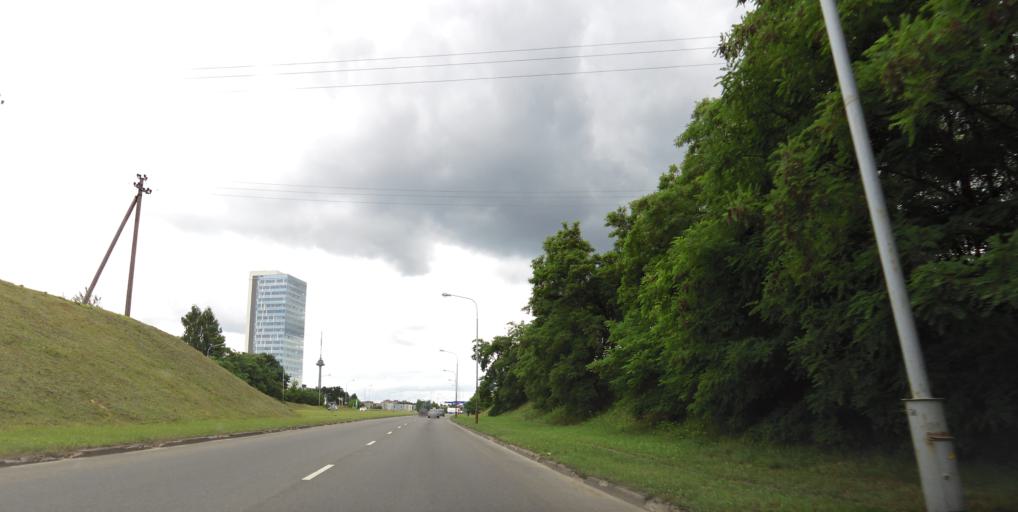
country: LT
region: Vilnius County
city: Justiniskes
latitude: 54.7055
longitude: 25.2096
